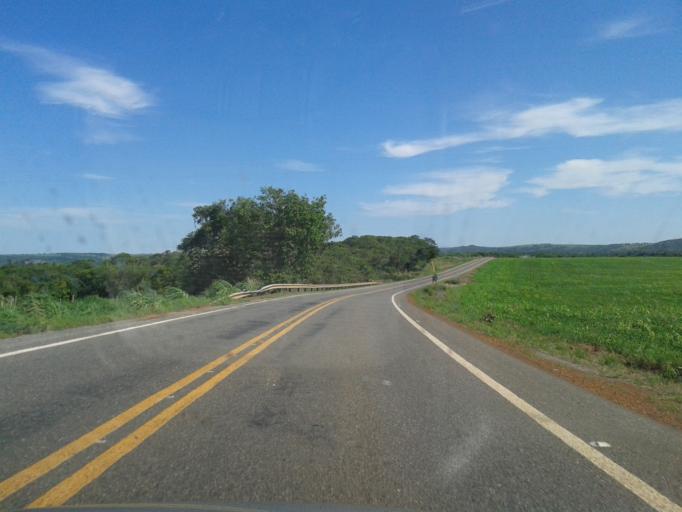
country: BR
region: Goias
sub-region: Piracanjuba
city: Piracanjuba
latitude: -17.3262
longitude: -48.8010
